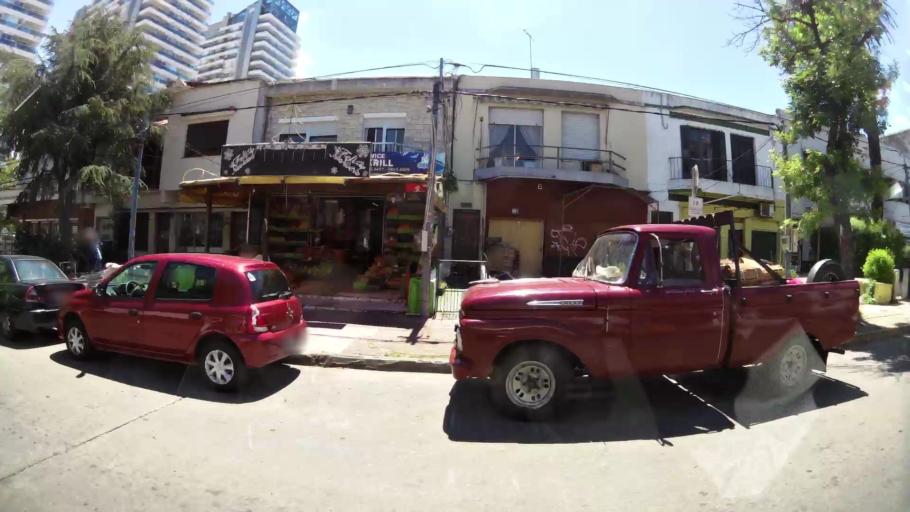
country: UY
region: Montevideo
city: Montevideo
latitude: -34.8962
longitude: -56.1213
